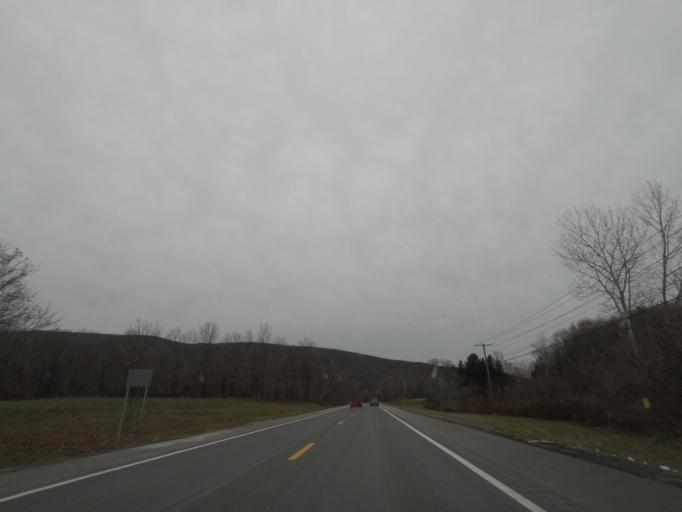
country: US
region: Massachusetts
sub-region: Berkshire County
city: Lanesborough
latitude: 42.5482
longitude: -73.3117
